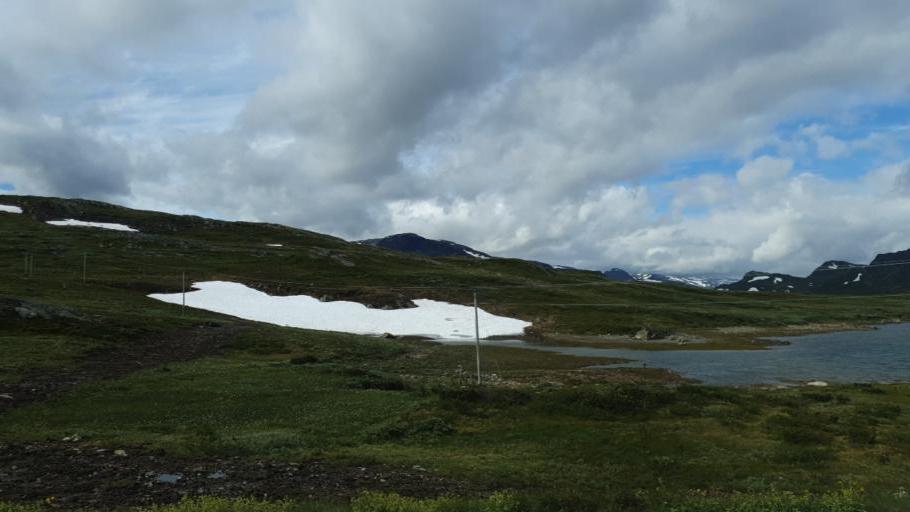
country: NO
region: Oppland
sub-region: Vestre Slidre
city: Slidre
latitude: 61.3269
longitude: 8.8013
